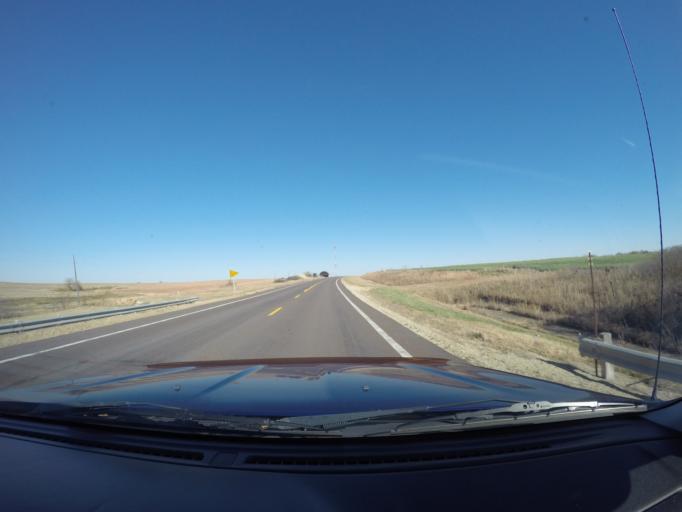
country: US
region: Kansas
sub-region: Marshall County
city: Blue Rapids
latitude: 39.5592
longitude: -96.7553
